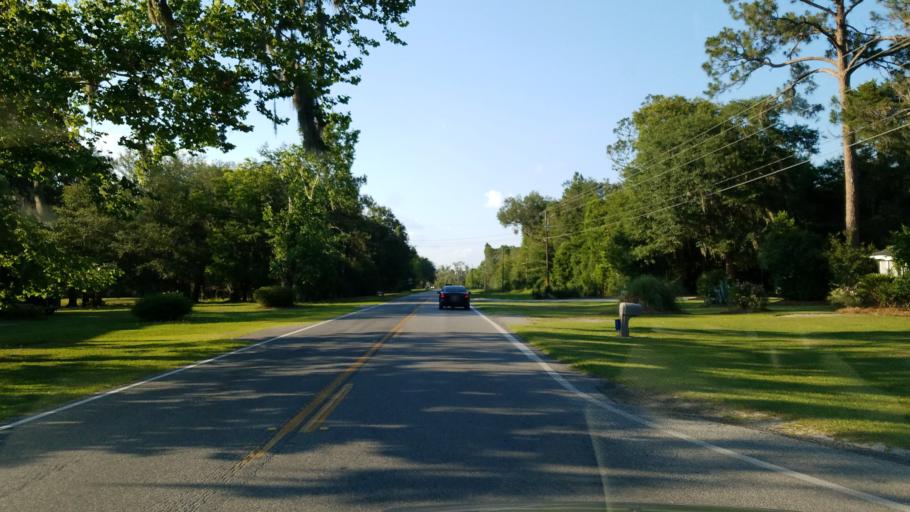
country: US
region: Georgia
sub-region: Lanier County
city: Lakeland
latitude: 31.0073
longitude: -83.0651
